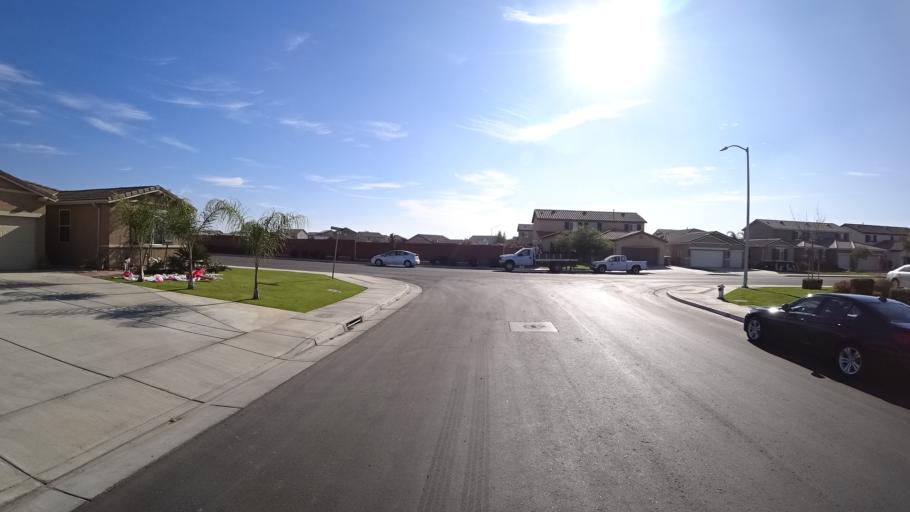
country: US
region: California
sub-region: Kern County
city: Greenfield
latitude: 35.2920
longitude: -119.0627
